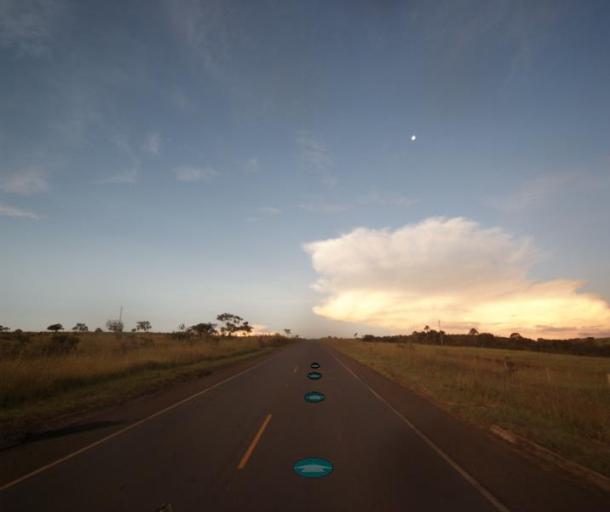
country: BR
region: Goias
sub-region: Pirenopolis
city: Pirenopolis
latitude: -16.0254
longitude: -48.8440
